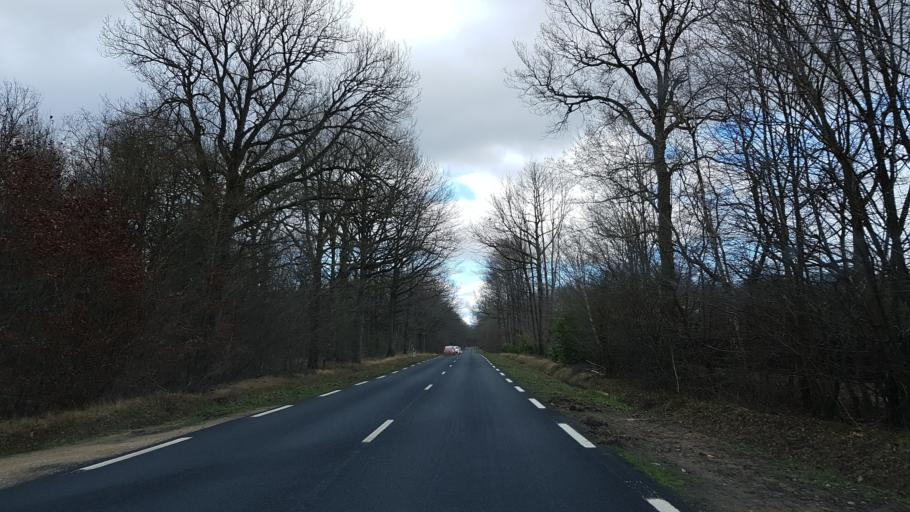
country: FR
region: Ile-de-France
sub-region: Departement des Yvelines
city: Sonchamp
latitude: 48.6305
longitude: 1.8860
